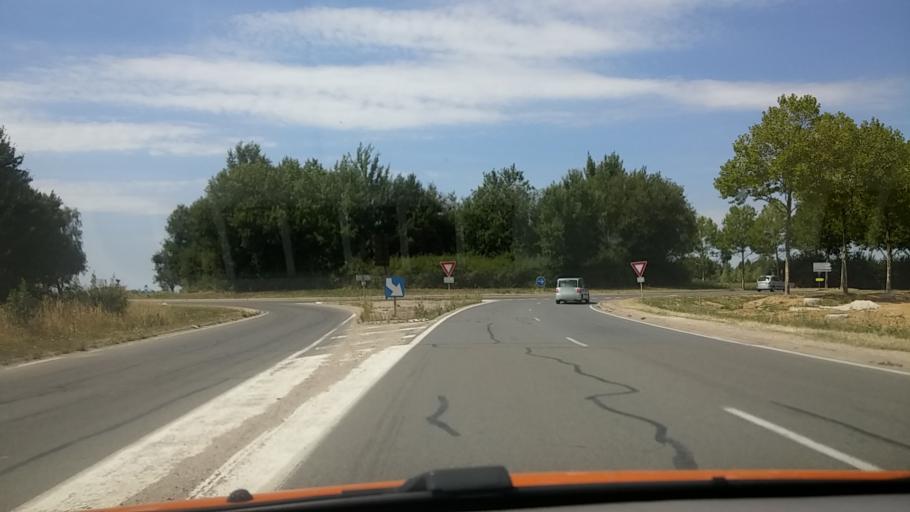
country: FR
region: Ile-de-France
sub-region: Departement de Seine-et-Marne
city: Serris
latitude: 48.8351
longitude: 2.7928
